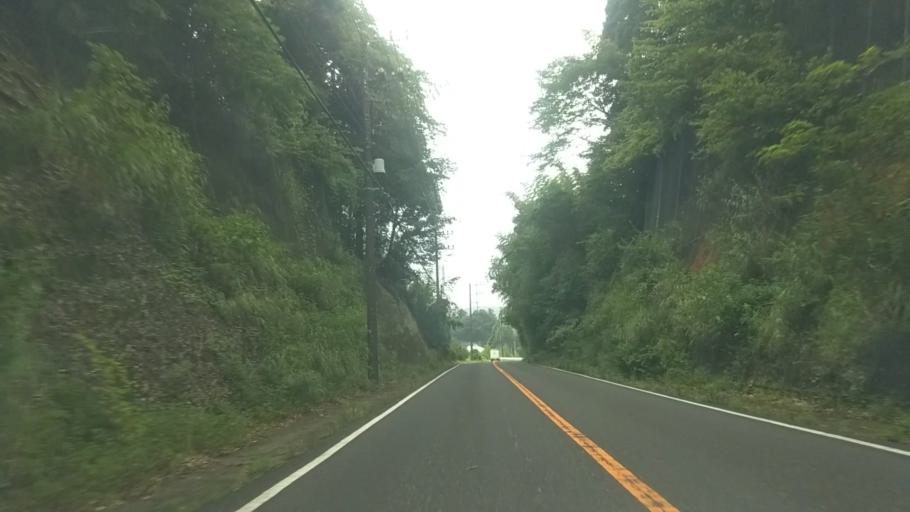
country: JP
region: Chiba
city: Kawaguchi
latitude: 35.2313
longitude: 140.0744
